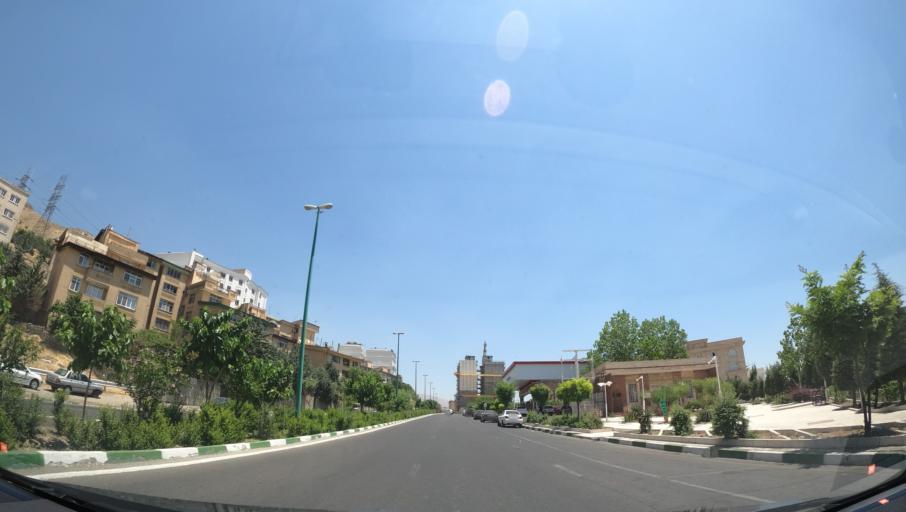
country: IR
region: Tehran
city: Tajrish
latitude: 35.8110
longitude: 51.3924
